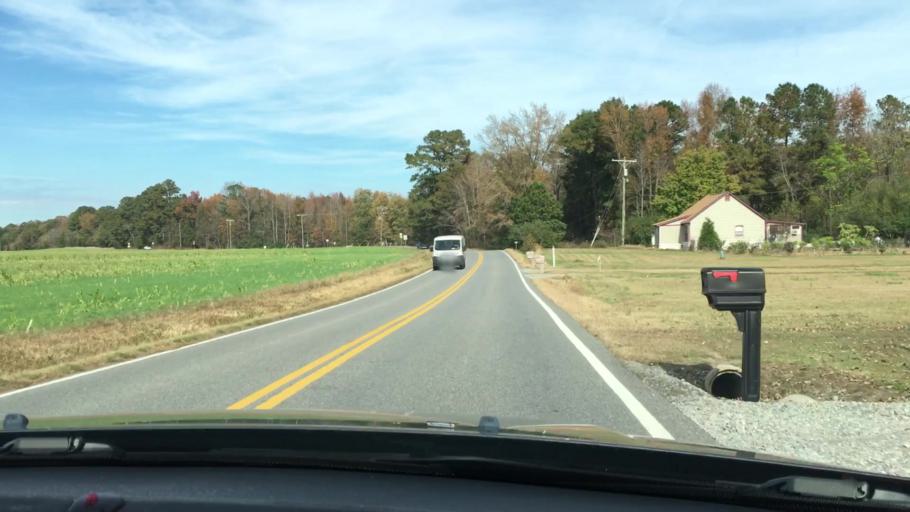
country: US
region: Virginia
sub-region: King William County
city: West Point
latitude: 37.5105
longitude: -76.8204
